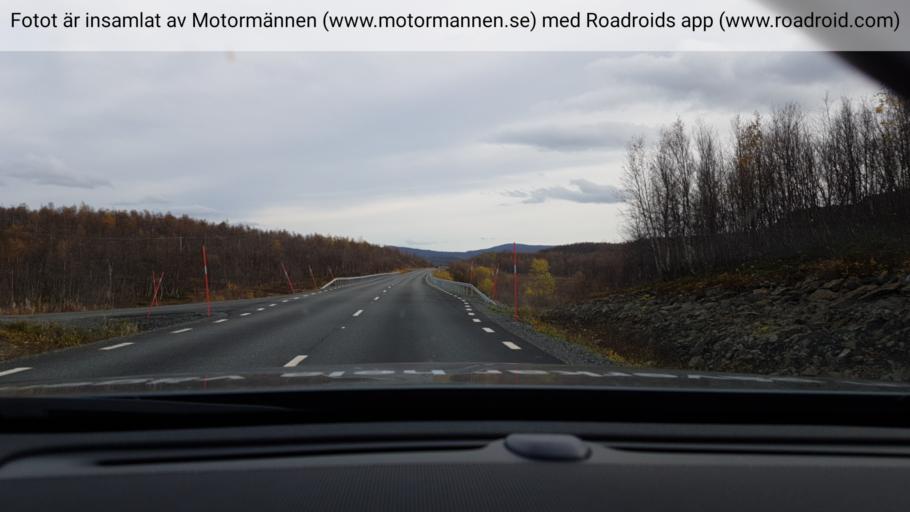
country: NO
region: Nordland
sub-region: Sorfold
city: Straumen
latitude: 66.5971
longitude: 16.2610
